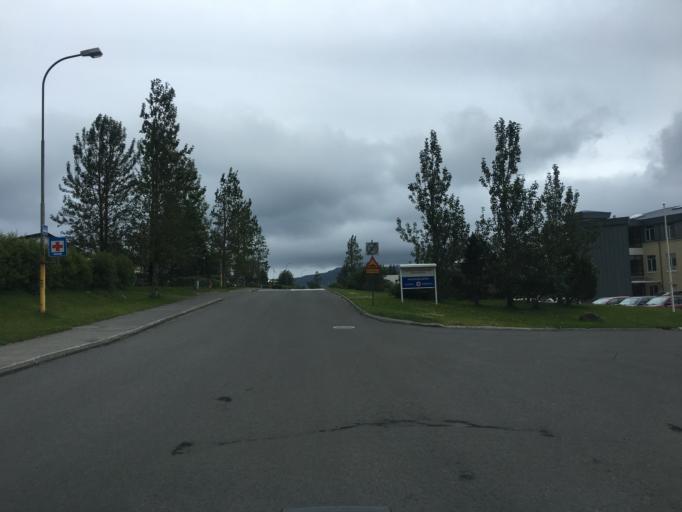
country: IS
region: East
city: Neskaupstadur
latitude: 65.1490
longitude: -13.6773
